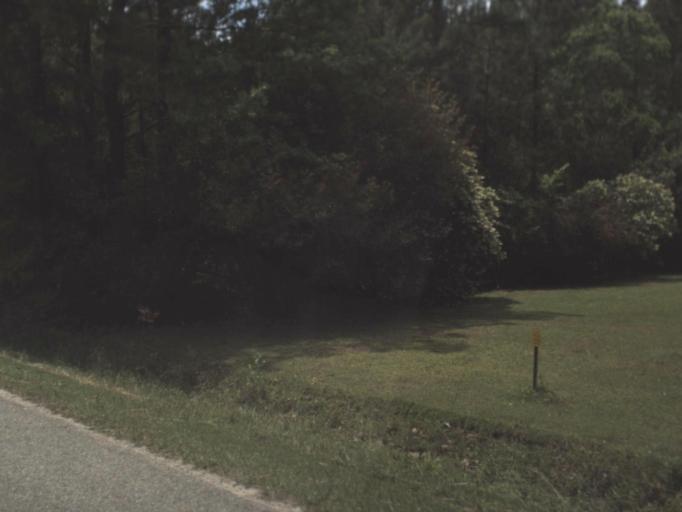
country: US
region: Florida
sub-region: Calhoun County
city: Blountstown
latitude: 30.5490
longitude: -85.1286
